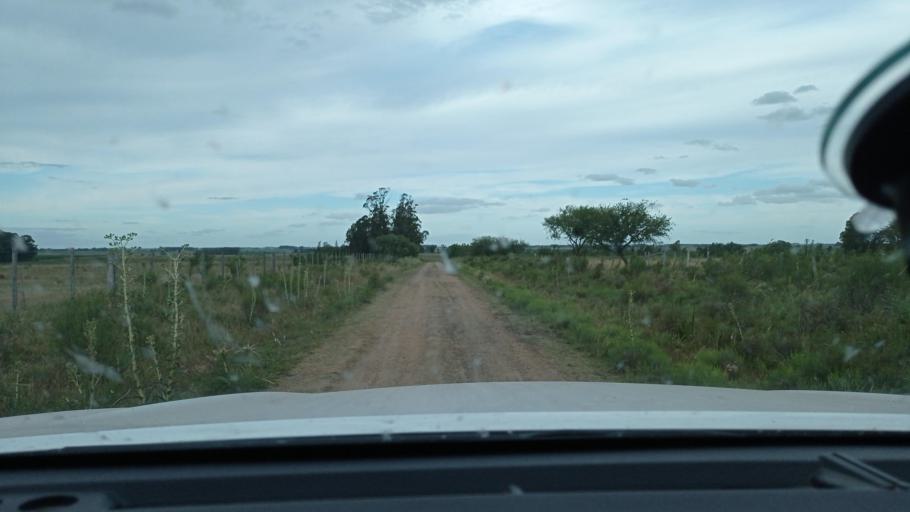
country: UY
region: Florida
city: Casupa
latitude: -34.1237
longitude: -55.8142
